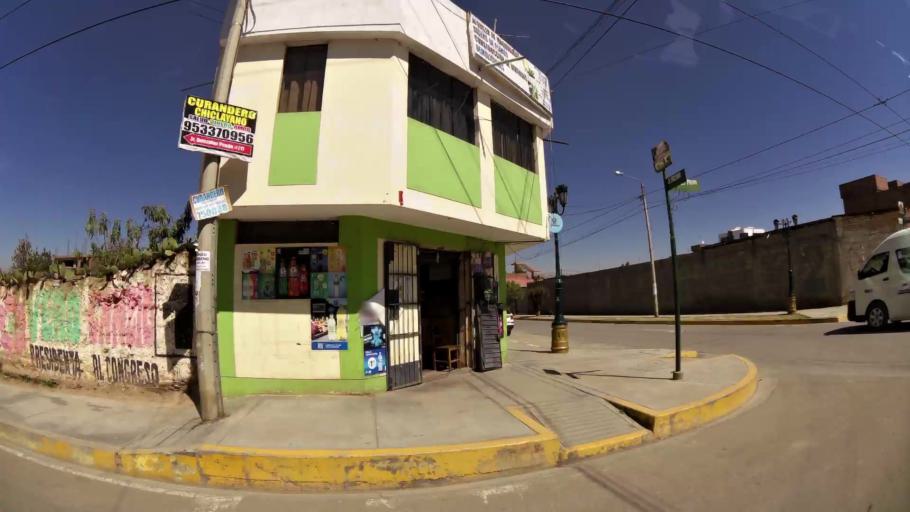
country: PE
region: Junin
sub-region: Provincia de Concepcion
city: Concepcion
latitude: -11.9194
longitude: -75.3157
